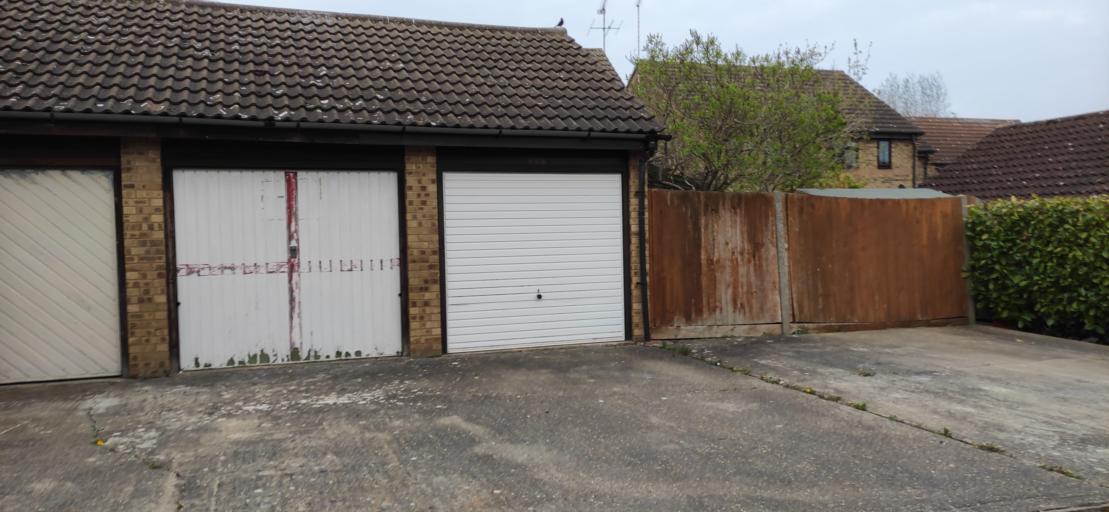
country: GB
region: England
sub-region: Cambridgeshire
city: Swavesey
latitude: 52.2503
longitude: 0.0169
